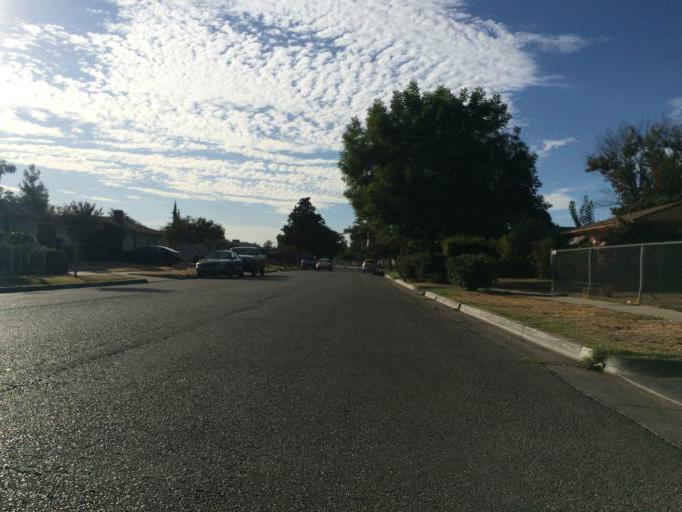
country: US
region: California
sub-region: Fresno County
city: Sunnyside
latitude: 36.7616
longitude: -119.7335
